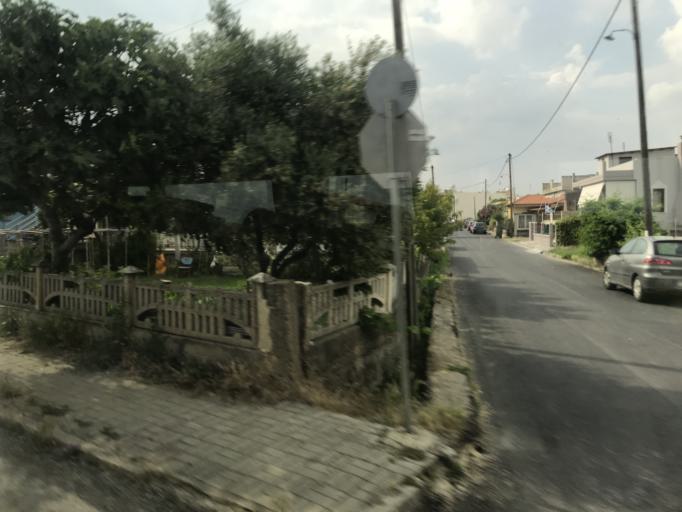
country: GR
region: East Macedonia and Thrace
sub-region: Nomos Evrou
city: Alexandroupoli
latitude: 40.8566
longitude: 25.9380
